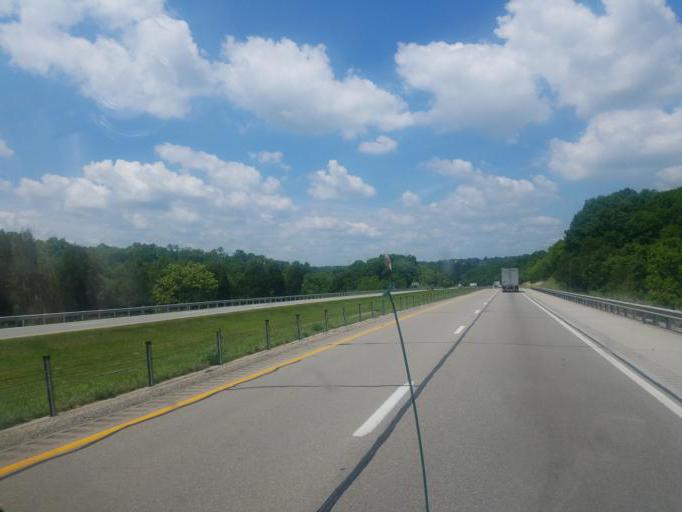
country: US
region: Indiana
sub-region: Switzerland County
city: Vevay
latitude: 38.6559
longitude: -85.0669
